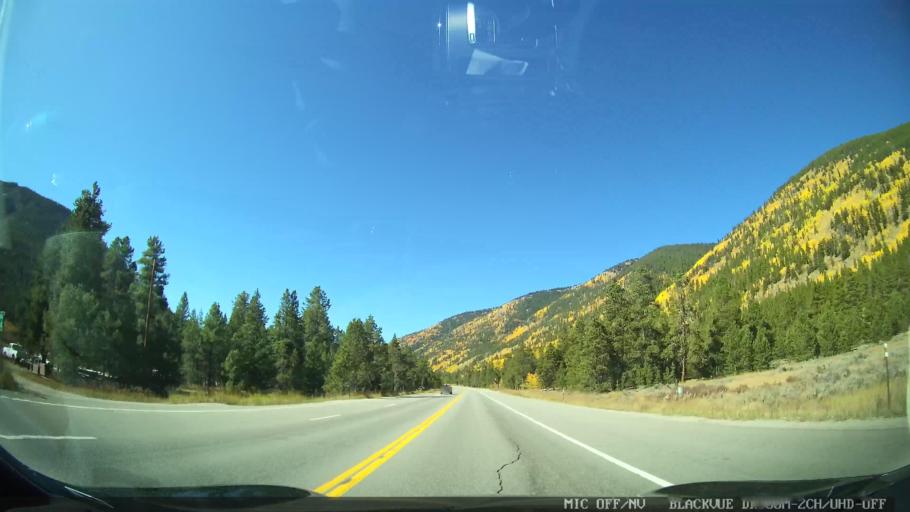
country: US
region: Colorado
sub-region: Lake County
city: Leadville
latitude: 39.3083
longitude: -106.2481
